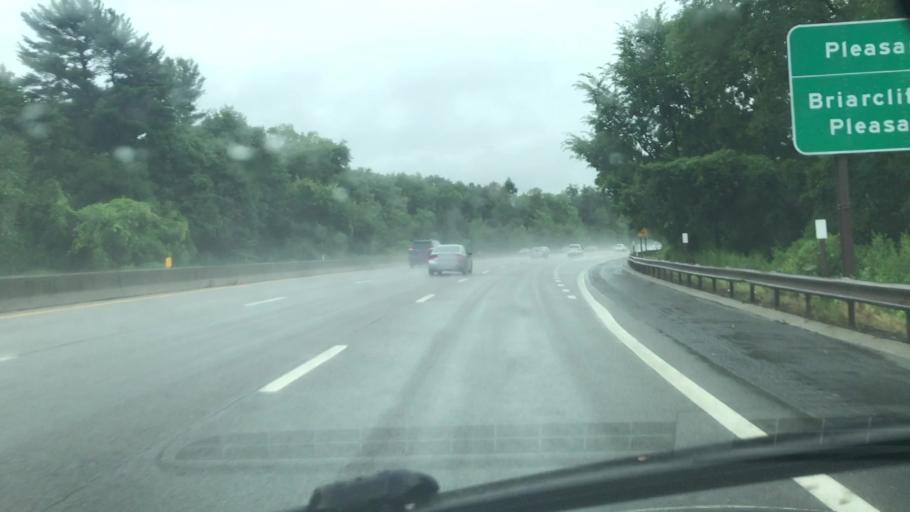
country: US
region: New York
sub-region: Westchester County
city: Briarcliff Manor
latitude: 41.1394
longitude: -73.8169
